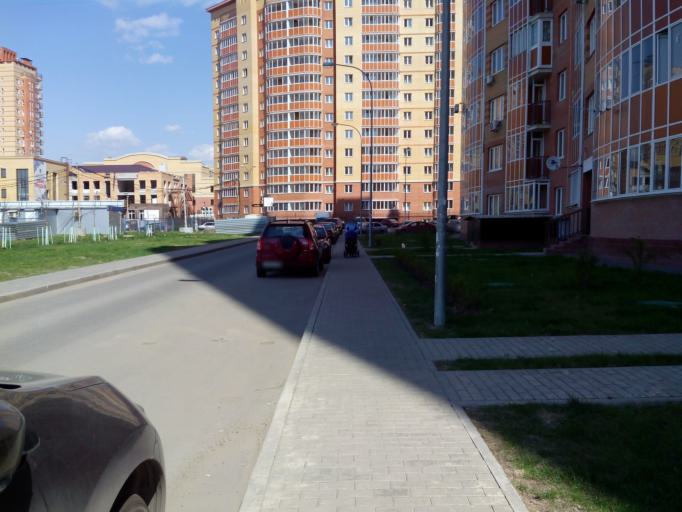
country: RU
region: Moskovskaya
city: Lesnoy Gorodok
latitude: 55.6585
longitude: 37.2283
